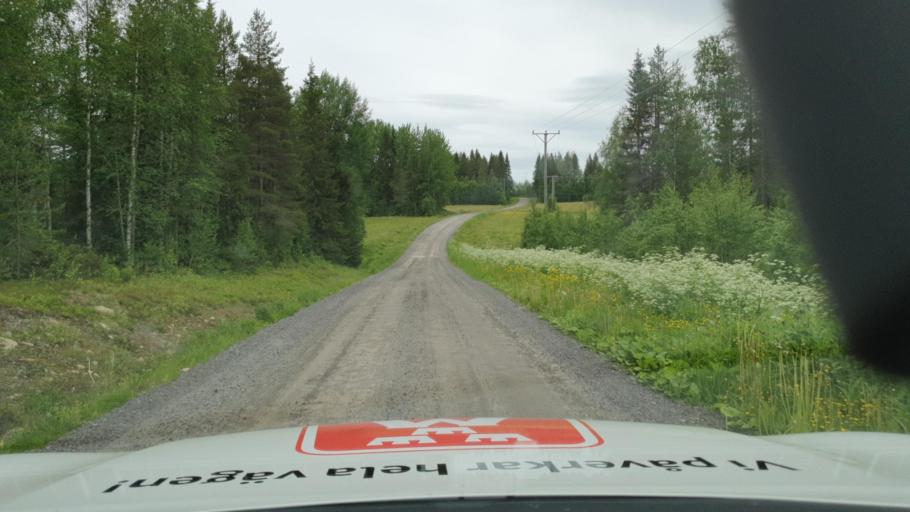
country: SE
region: Vaesterbotten
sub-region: Skelleftea Kommun
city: Burtraesk
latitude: 64.3603
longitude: 20.6158
